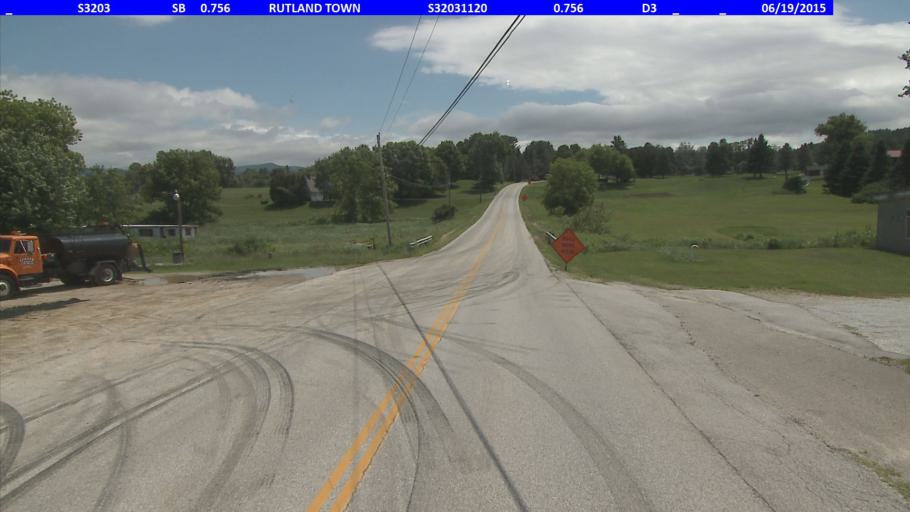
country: US
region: Vermont
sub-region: Rutland County
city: Rutland
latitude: 43.6637
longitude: -73.0008
